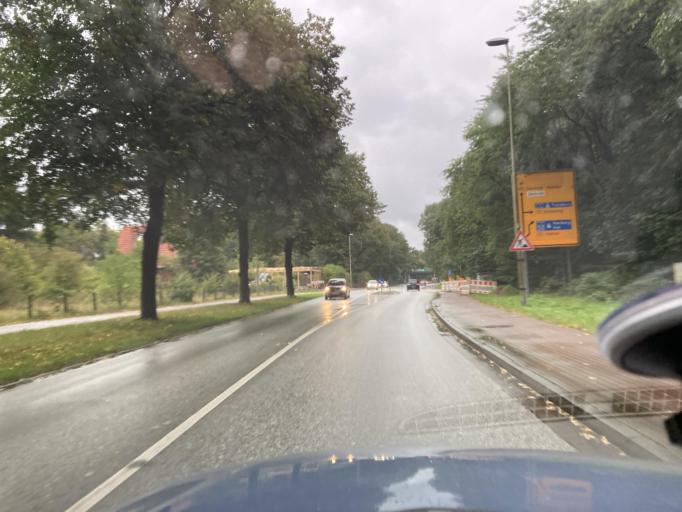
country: DE
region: Schleswig-Holstein
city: Fockbek
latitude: 54.3100
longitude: 9.6228
